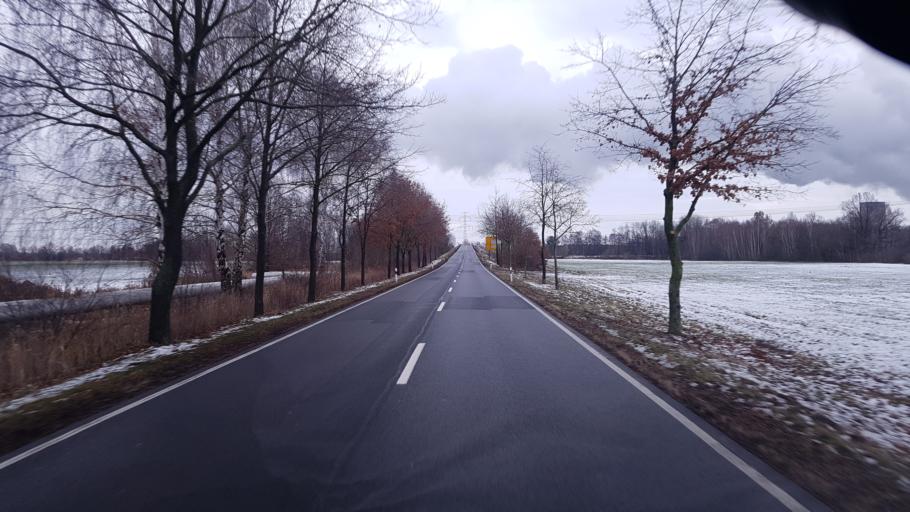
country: DE
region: Brandenburg
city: Peitz
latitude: 51.8502
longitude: 14.4459
